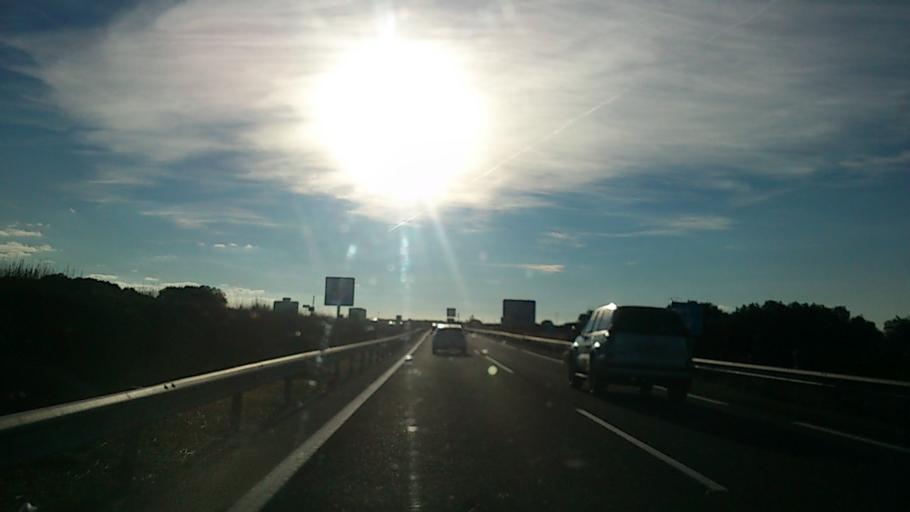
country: ES
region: Castille-La Mancha
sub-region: Provincia de Guadalajara
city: Mirabueno
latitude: 40.9358
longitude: -2.7062
